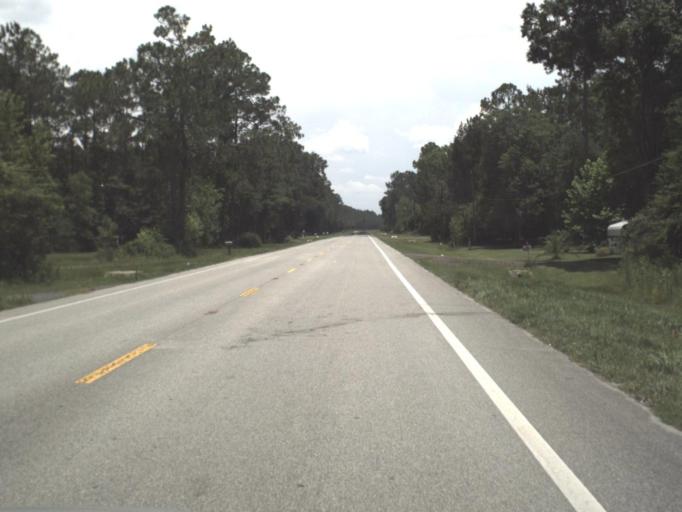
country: US
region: Florida
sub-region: Bradford County
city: Starke
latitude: 29.9935
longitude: -82.1308
